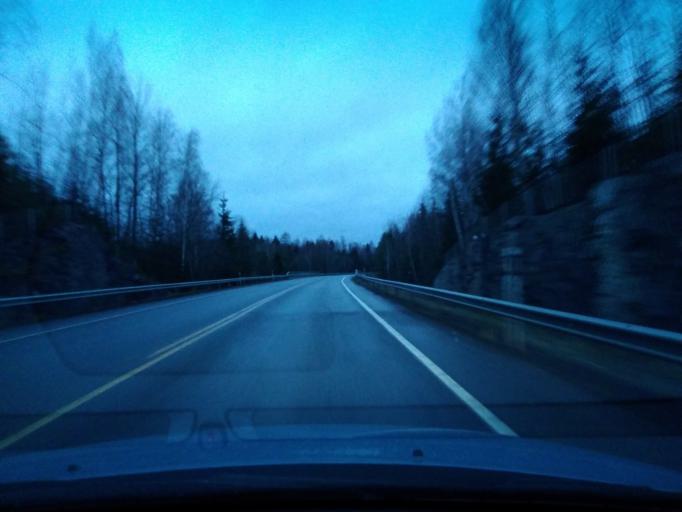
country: FI
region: Uusimaa
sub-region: Porvoo
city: Porvoo
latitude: 60.4071
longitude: 25.5863
